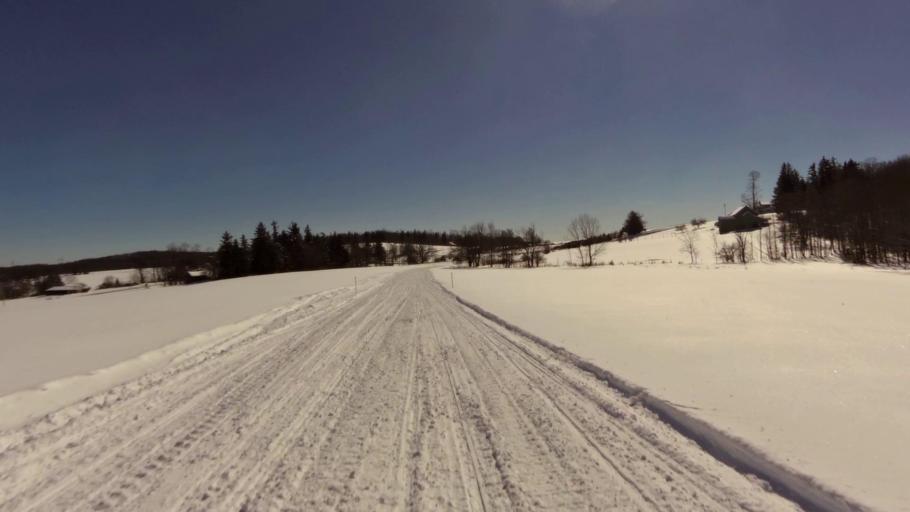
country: US
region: New York
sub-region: Chautauqua County
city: Mayville
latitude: 42.2208
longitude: -79.5189
